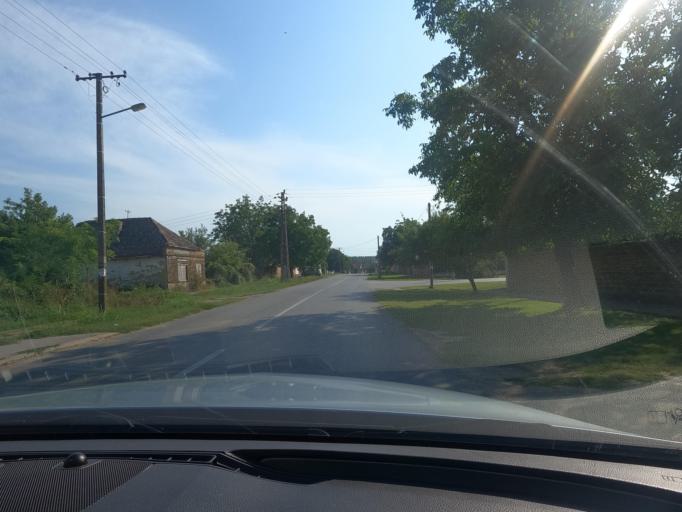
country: RS
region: Autonomna Pokrajina Vojvodina
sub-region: Juznobacki Okrug
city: Kovilj
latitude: 45.2195
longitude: 20.0342
